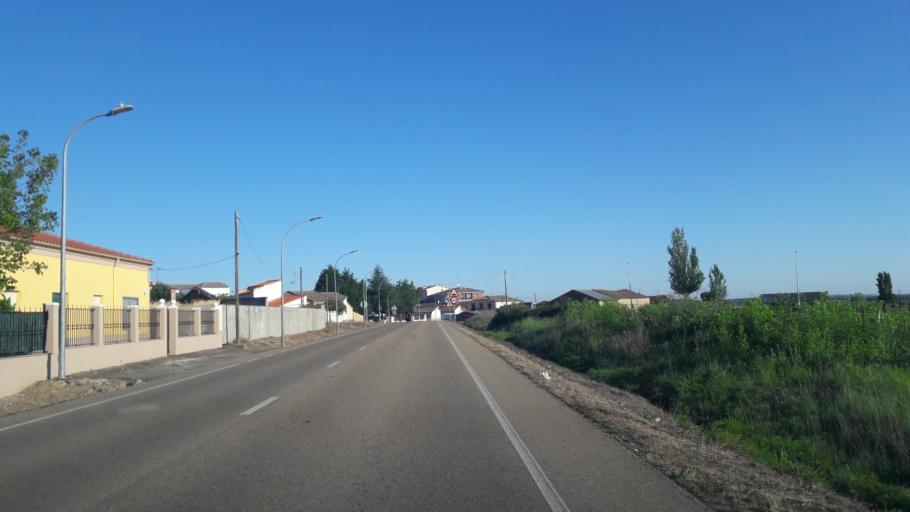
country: ES
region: Castille and Leon
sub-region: Provincia de Salamanca
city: La Fuente de San Esteban
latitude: 40.8010
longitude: -6.2540
